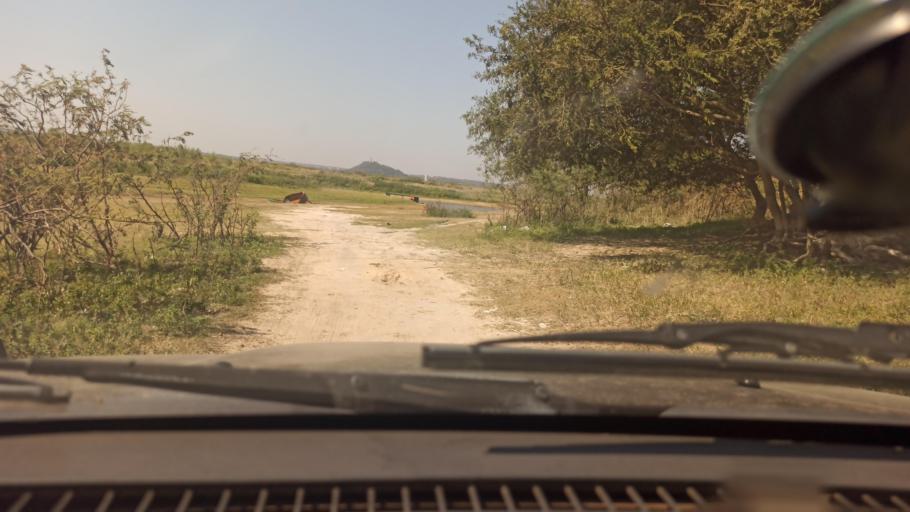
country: PY
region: Asuncion
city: Asuncion
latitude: -25.3284
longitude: -57.6813
